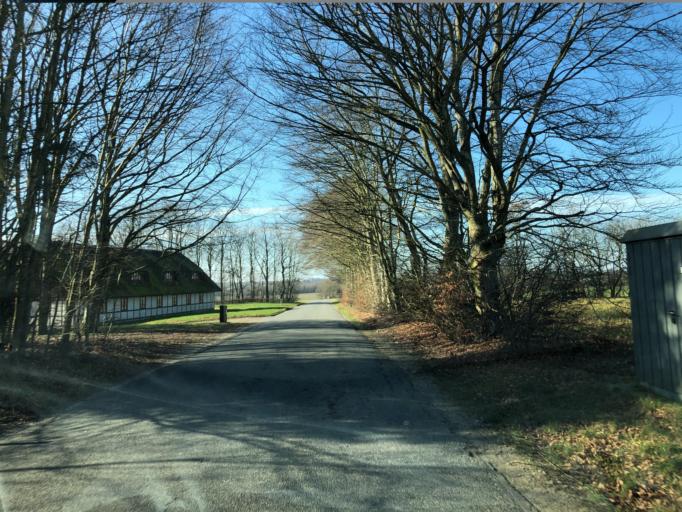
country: DK
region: Central Jutland
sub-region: Ikast-Brande Kommune
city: Bording Kirkeby
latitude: 56.1530
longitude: 9.2874
